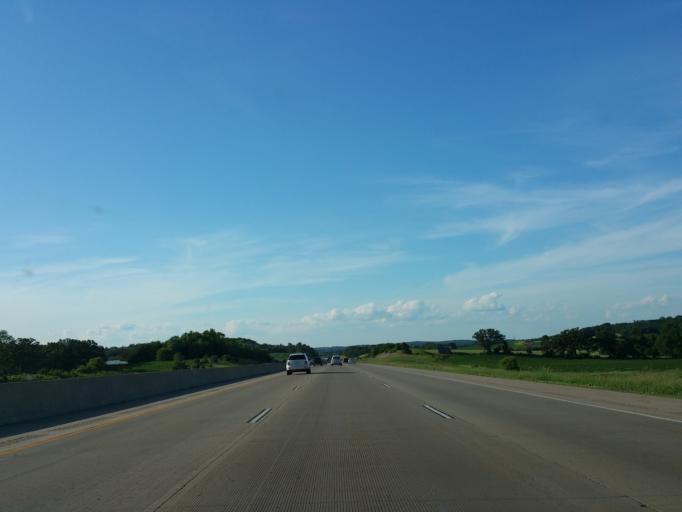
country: US
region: Wisconsin
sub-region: Columbia County
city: Poynette
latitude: 43.3531
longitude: -89.4593
